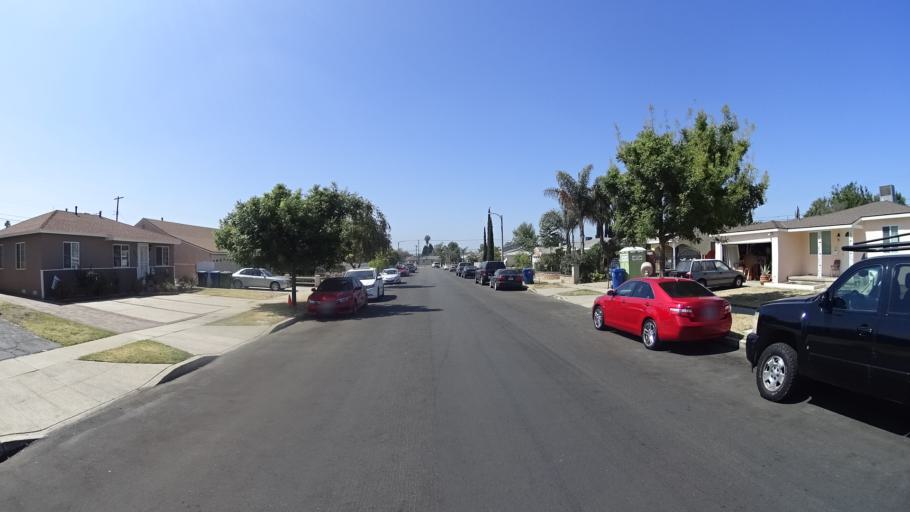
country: US
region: California
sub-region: Los Angeles County
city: Van Nuys
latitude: 34.2312
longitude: -118.4438
